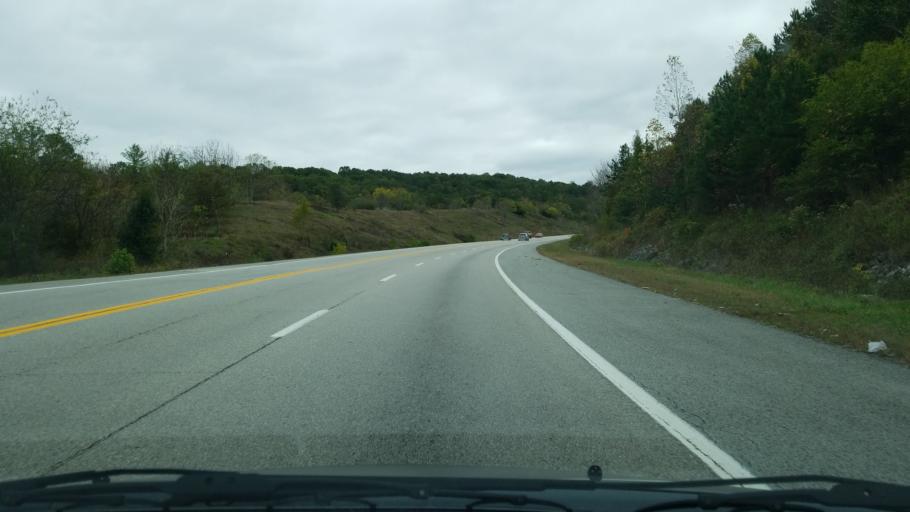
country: US
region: Tennessee
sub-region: Rhea County
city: Dayton
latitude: 35.4780
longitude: -85.0215
